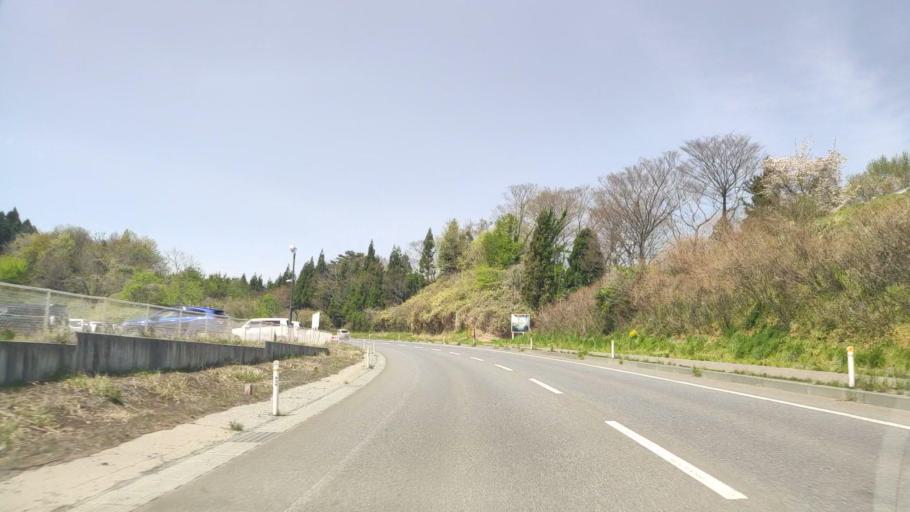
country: JP
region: Aomori
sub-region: Hachinohe Shi
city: Uchimaru
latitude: 40.5209
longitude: 141.4252
